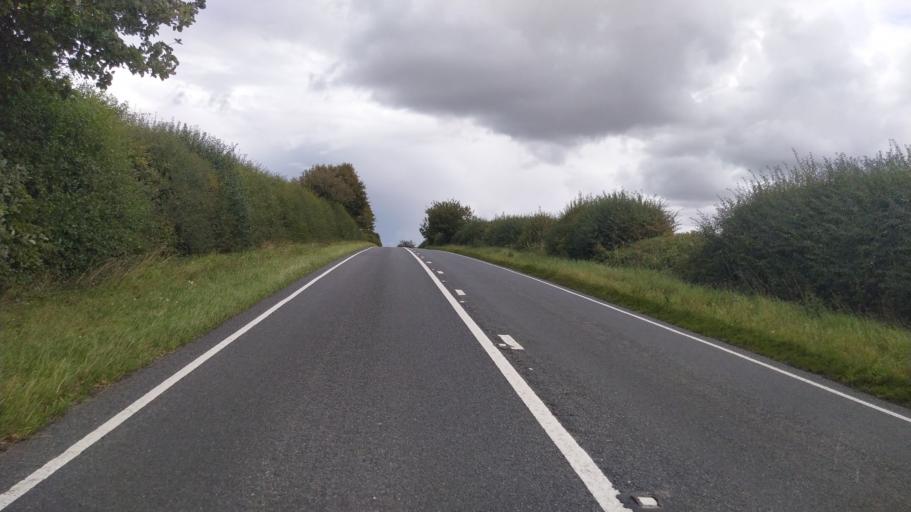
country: GB
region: England
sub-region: Dorset
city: Blandford Forum
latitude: 50.9009
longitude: -2.0801
